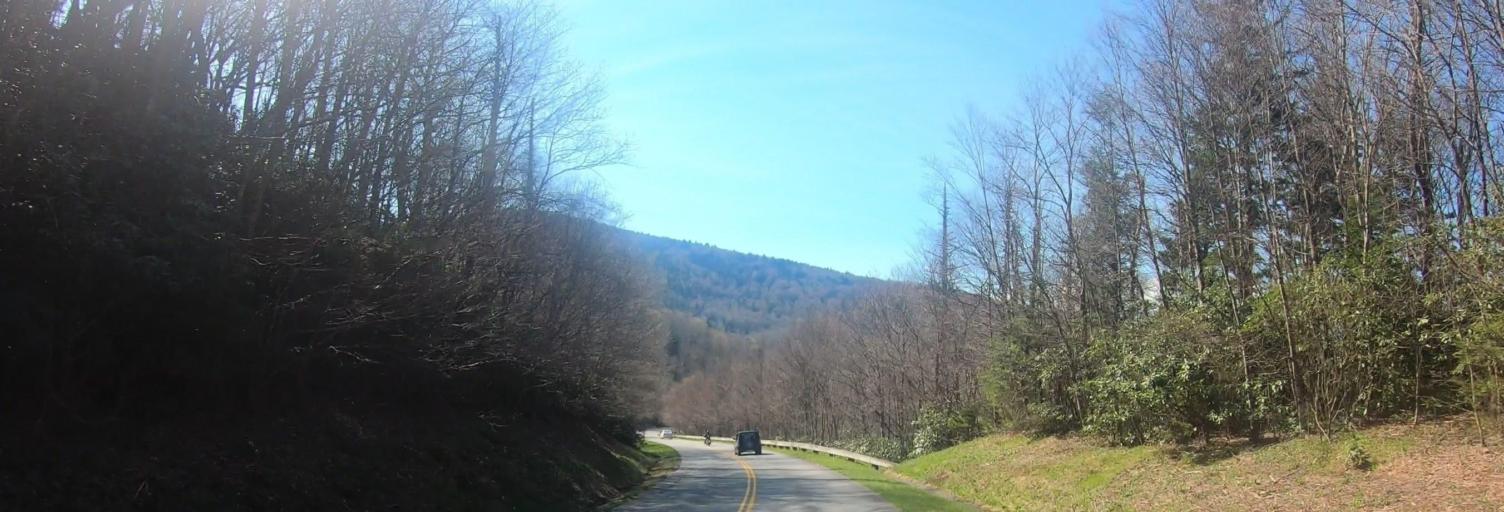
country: US
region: North Carolina
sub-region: Watauga County
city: Foscoe
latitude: 36.1040
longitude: -81.7821
